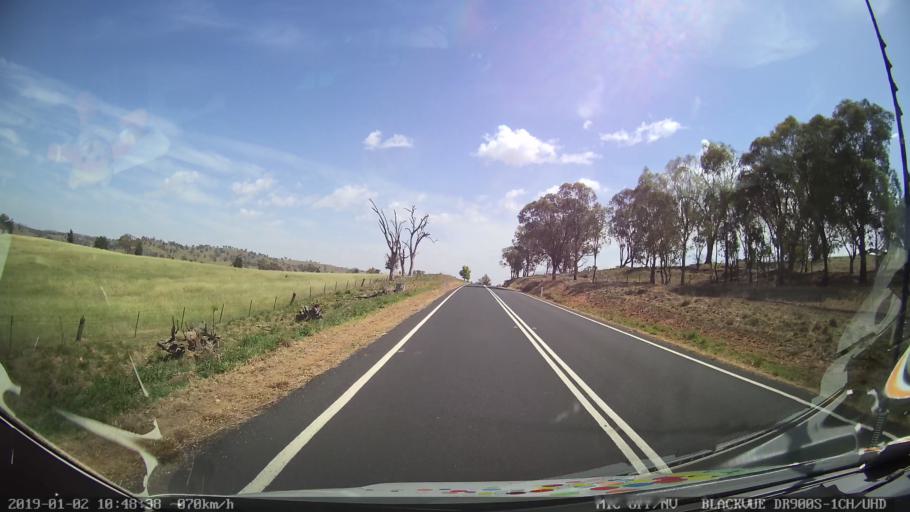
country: AU
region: New South Wales
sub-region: Cootamundra
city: Cootamundra
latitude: -34.7345
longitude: 148.2777
